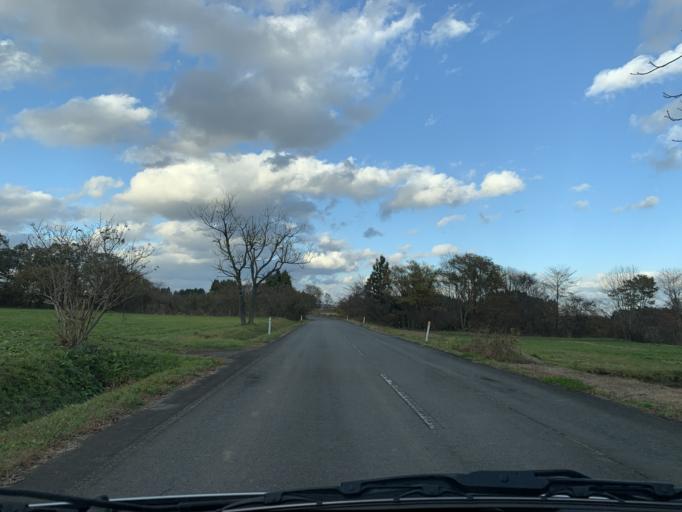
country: JP
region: Iwate
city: Mizusawa
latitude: 39.0942
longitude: 141.0122
